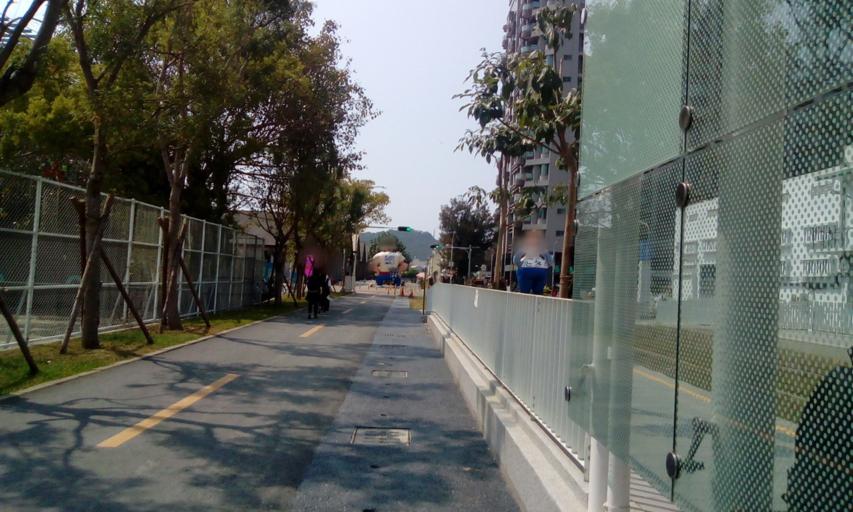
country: TW
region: Kaohsiung
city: Kaohsiung
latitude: 22.6205
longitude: 120.2799
